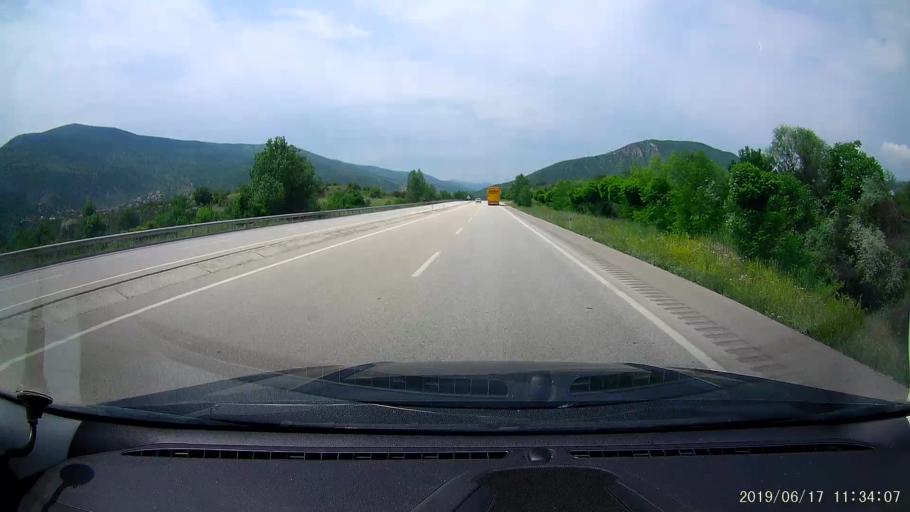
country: TR
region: Cankiri
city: Beloren
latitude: 40.8733
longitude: 33.4987
